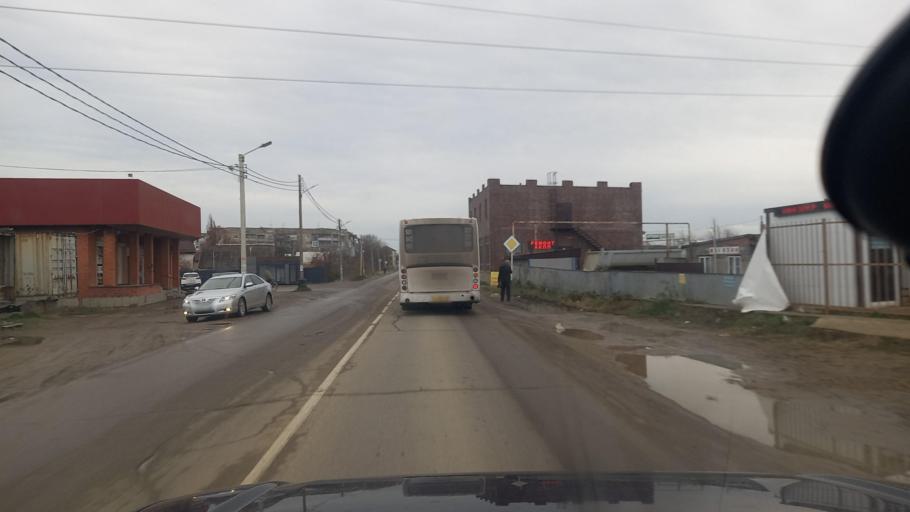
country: RU
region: Adygeya
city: Yablonovskiy
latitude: 44.9801
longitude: 38.9304
